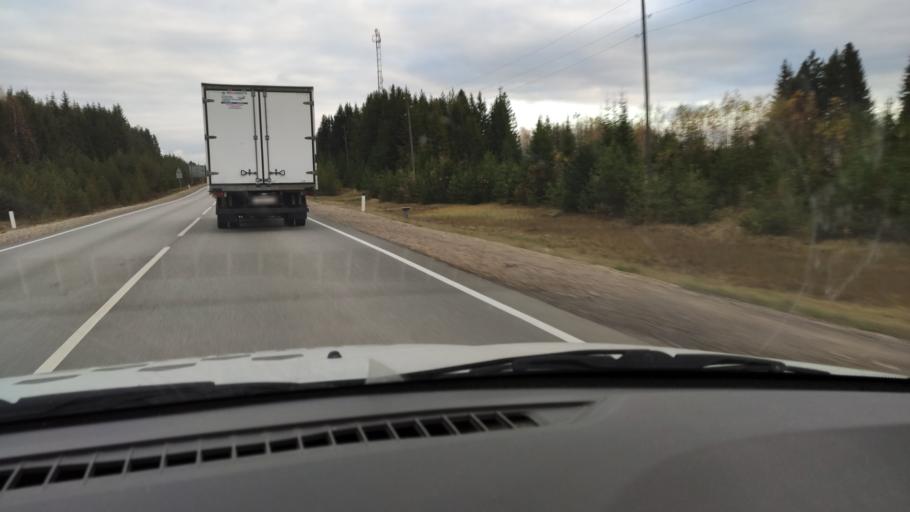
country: RU
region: Kirov
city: Chernaya Kholunitsa
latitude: 58.8563
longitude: 51.7231
